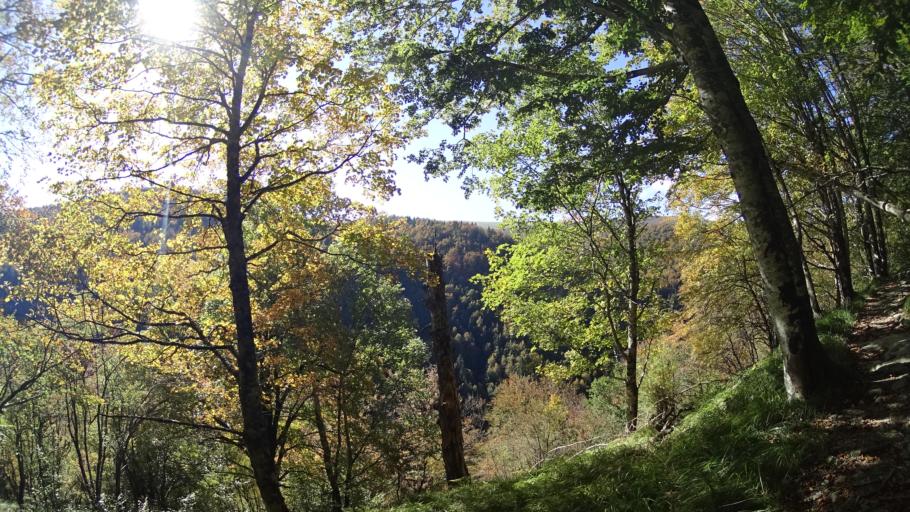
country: ES
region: Navarre
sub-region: Provincia de Navarra
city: Oronz
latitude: 42.9841
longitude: -1.1150
